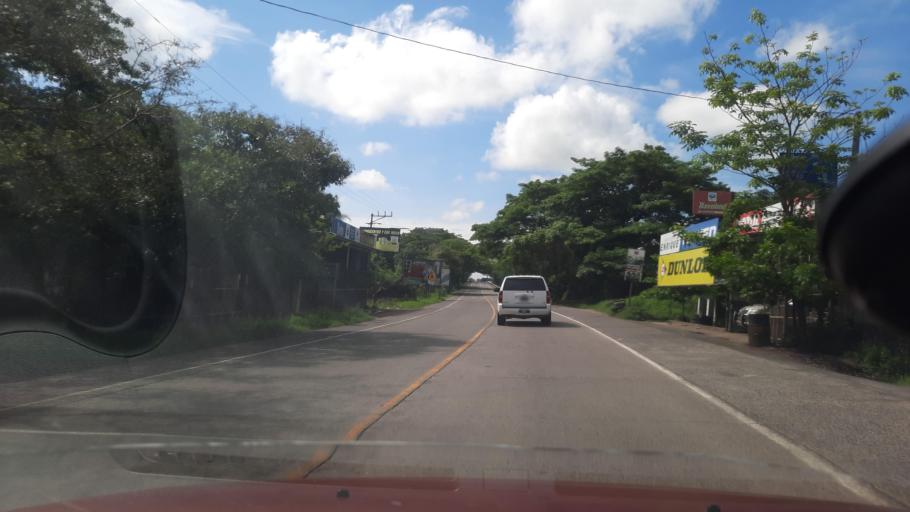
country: SV
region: Usulutan
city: San Agustin
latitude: 13.4284
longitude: -88.7041
